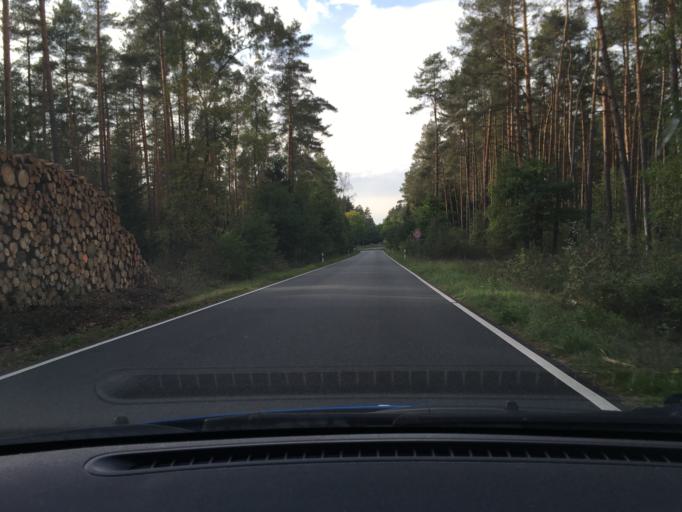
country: DE
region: Lower Saxony
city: Fassberg
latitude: 52.9061
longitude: 10.0970
